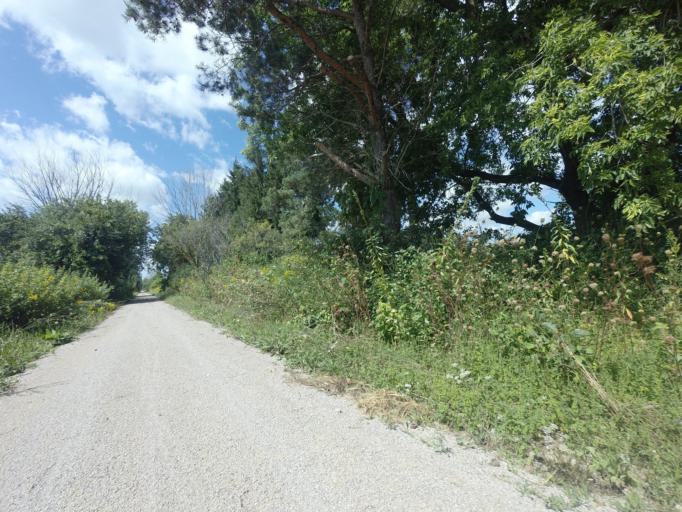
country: CA
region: Ontario
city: Huron East
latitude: 43.6282
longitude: -81.1733
